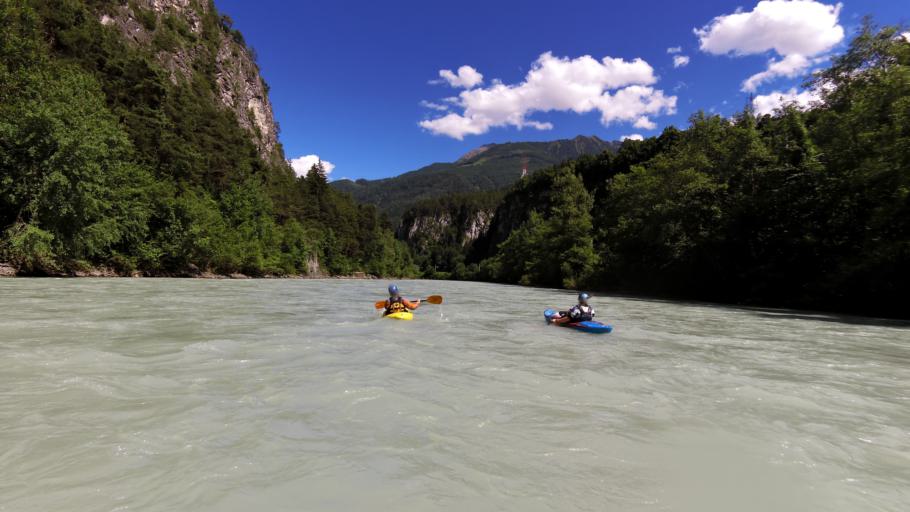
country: AT
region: Tyrol
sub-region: Politischer Bezirk Imst
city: Karres
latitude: 47.2129
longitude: 10.7831
